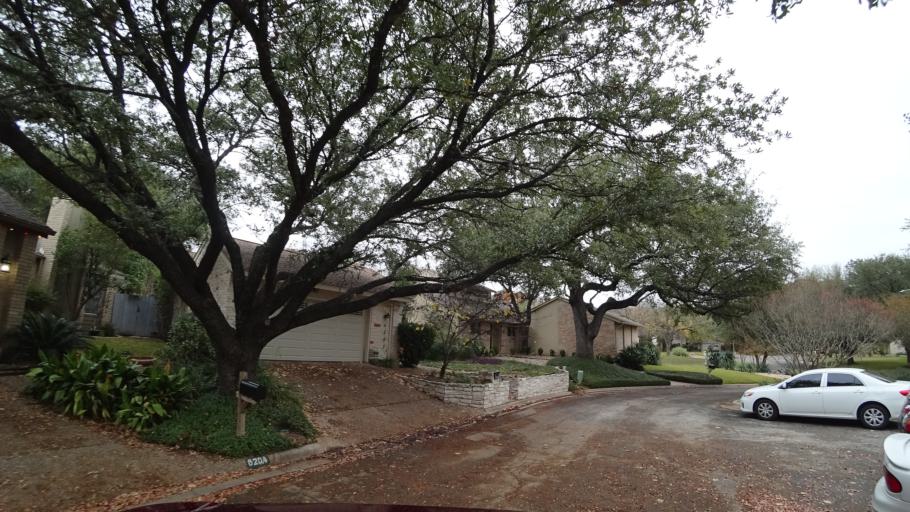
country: US
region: Texas
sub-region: Williamson County
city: Jollyville
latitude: 30.3739
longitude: -97.7877
